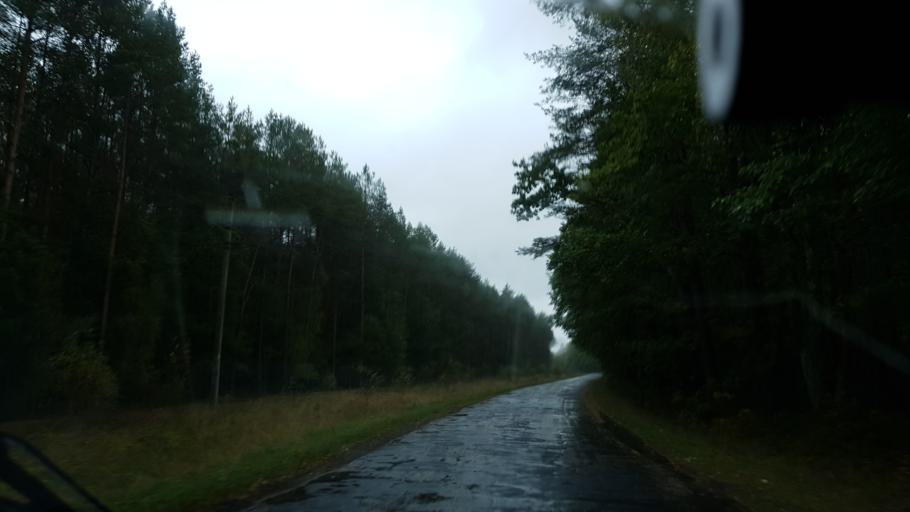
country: PL
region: West Pomeranian Voivodeship
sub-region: Powiat goleniowski
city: Przybiernow
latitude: 53.6741
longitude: 14.7290
